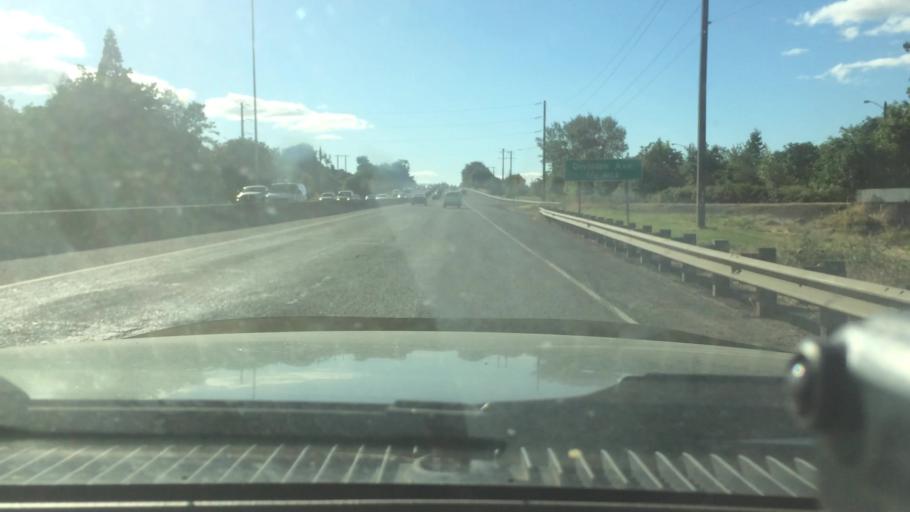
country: US
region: Oregon
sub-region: Lane County
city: Eugene
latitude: 44.0927
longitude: -123.1018
